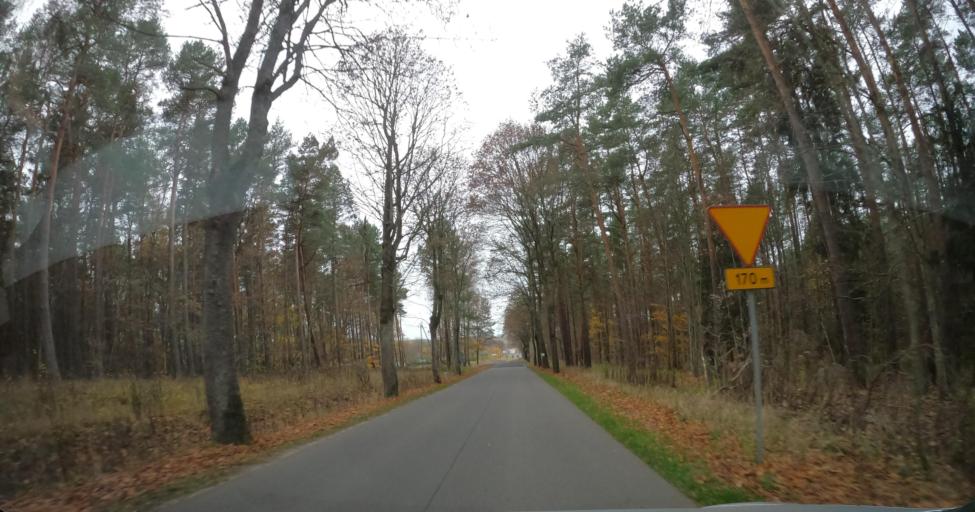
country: PL
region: West Pomeranian Voivodeship
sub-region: Powiat swidwinski
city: Polczyn-Zdroj
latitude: 53.7726
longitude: 16.1551
